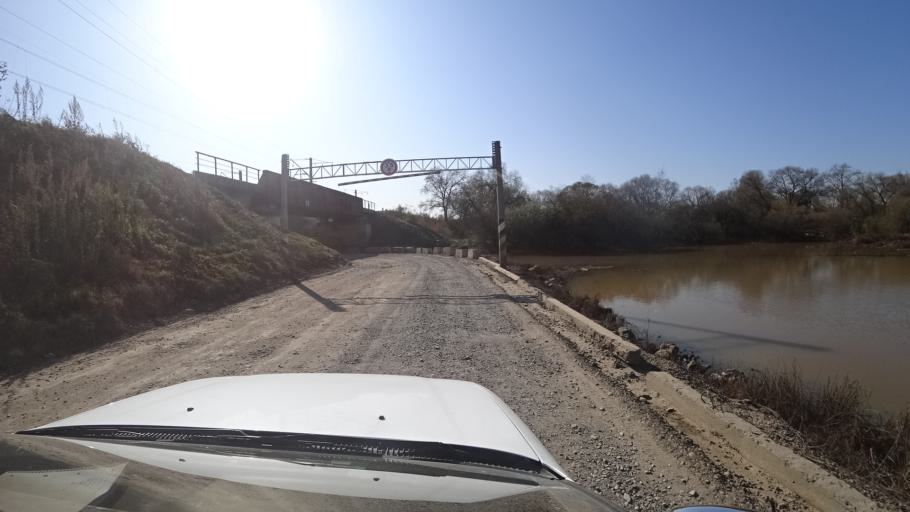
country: RU
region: Primorskiy
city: Dal'nerechensk
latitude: 45.9327
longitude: 133.7157
